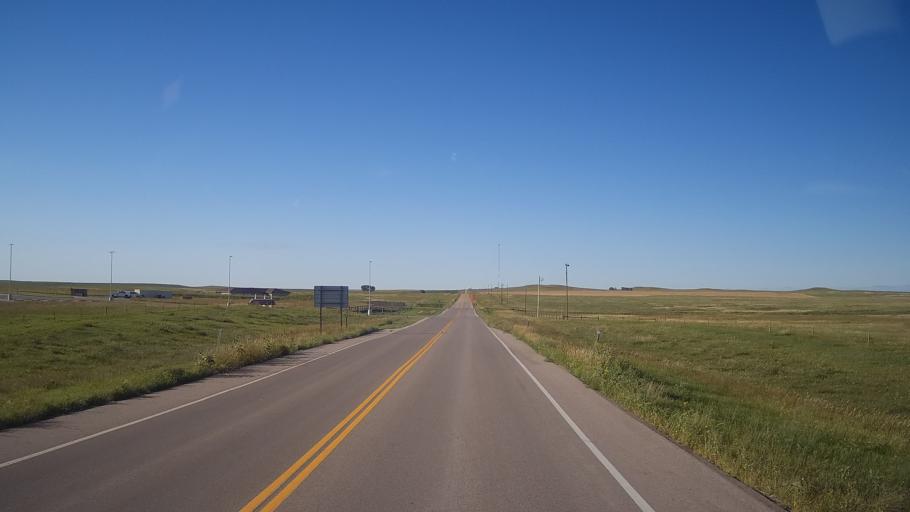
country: US
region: South Dakota
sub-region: Haakon County
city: Philip
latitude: 43.8431
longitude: -101.8998
